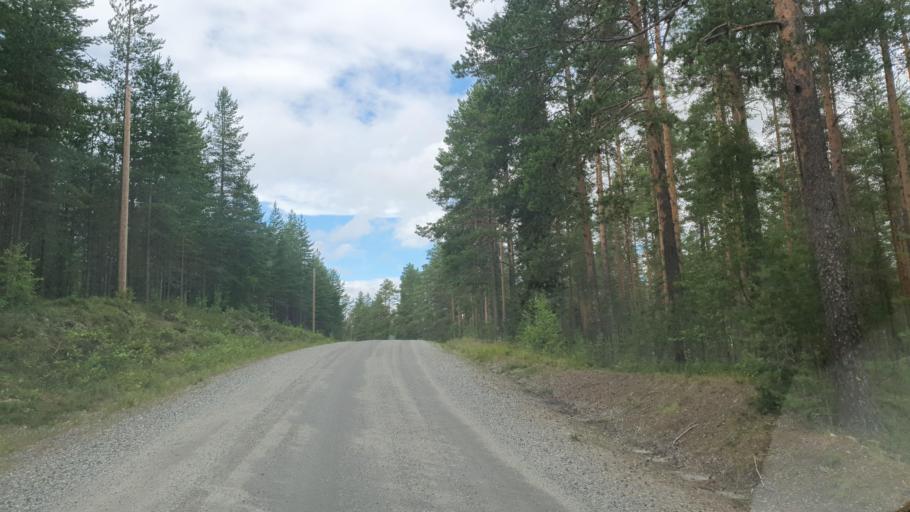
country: FI
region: Kainuu
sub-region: Kehys-Kainuu
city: Kuhmo
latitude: 64.1034
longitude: 29.4003
